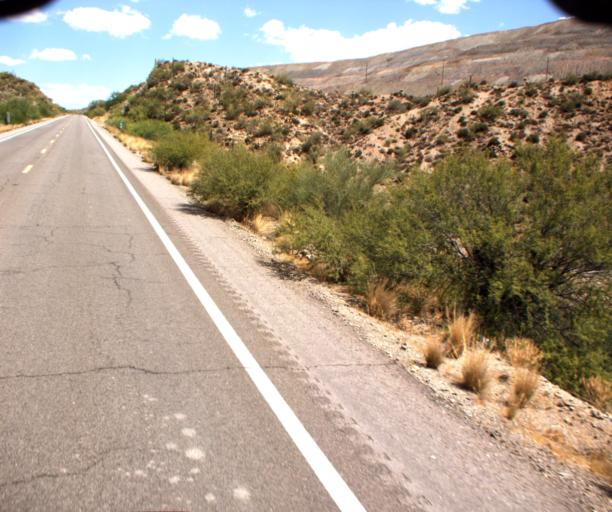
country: US
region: Arizona
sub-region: Pinal County
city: Kearny
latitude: 33.1418
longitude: -110.9909
